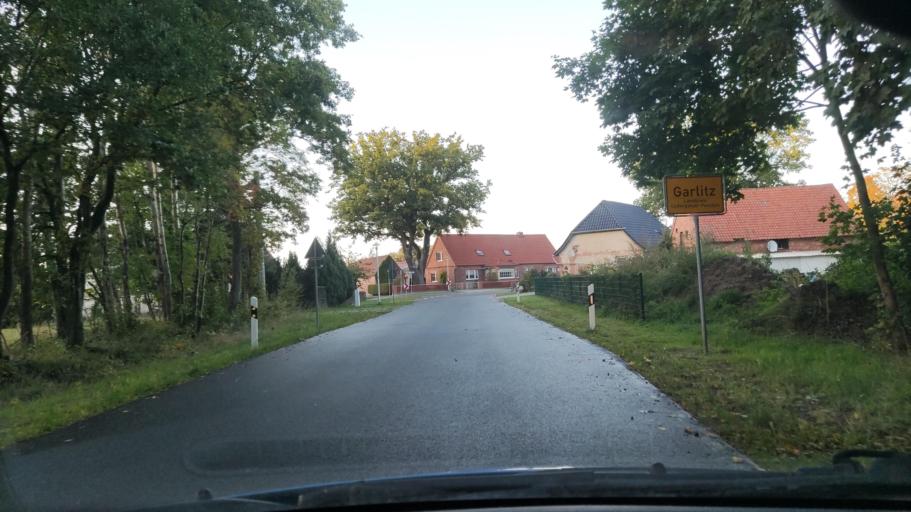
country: DE
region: Mecklenburg-Vorpommern
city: Lubtheen
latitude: 53.3126
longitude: 11.0042
